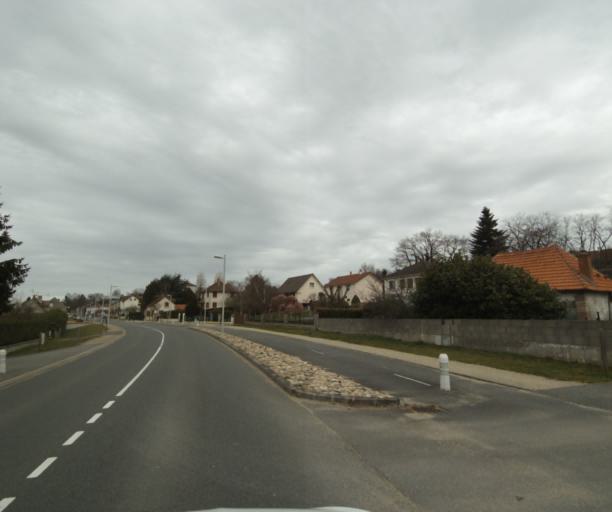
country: FR
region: Auvergne
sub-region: Departement de l'Allier
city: Toulon-sur-Allier
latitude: 46.5156
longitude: 3.3594
